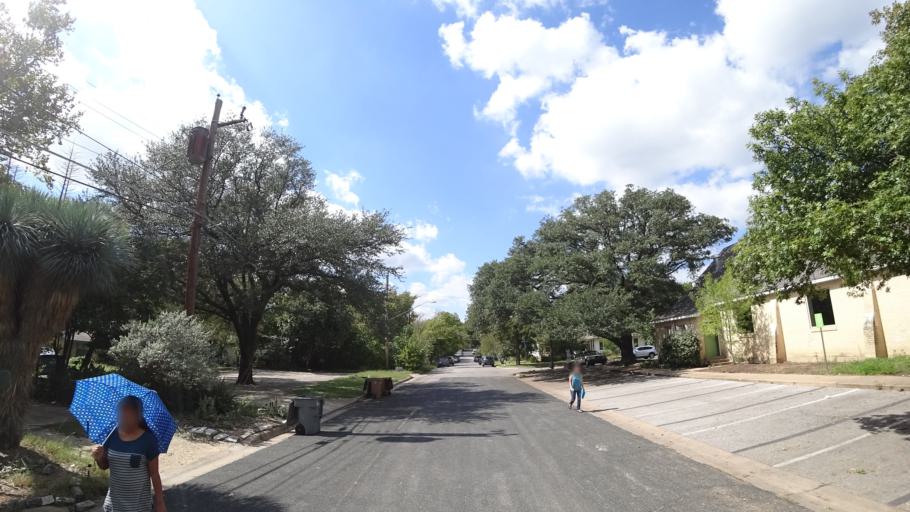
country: US
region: Texas
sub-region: Travis County
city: Austin
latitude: 30.3126
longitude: -97.7194
